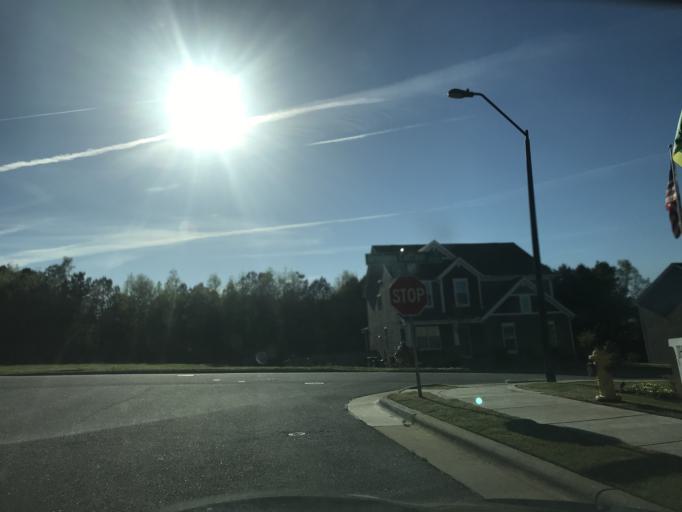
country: US
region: North Carolina
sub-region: Wake County
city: Knightdale
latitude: 35.8347
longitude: -78.5553
